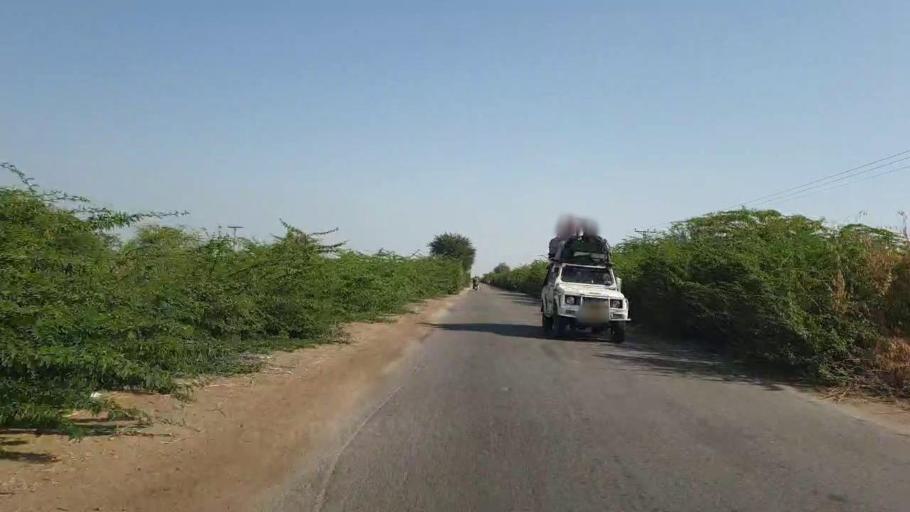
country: PK
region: Sindh
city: Chor
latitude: 25.4712
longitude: 69.7706
